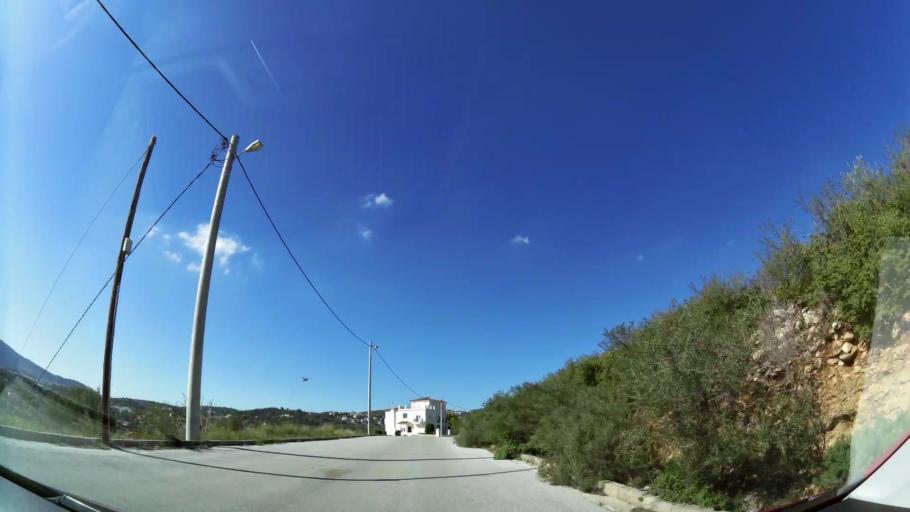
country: GR
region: Attica
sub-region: Nomarchia Anatolikis Attikis
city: Dhrafi
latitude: 38.0090
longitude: 23.9146
